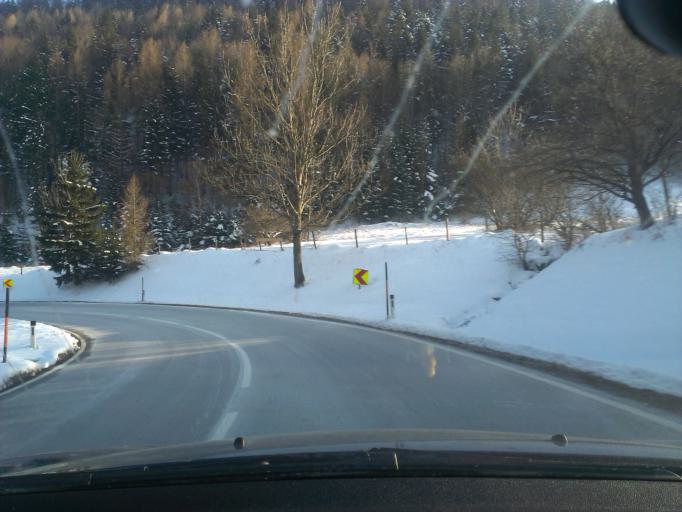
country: AT
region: Lower Austria
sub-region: Politischer Bezirk Wiener Neustadt
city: Miesenbach
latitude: 47.8184
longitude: 15.9517
